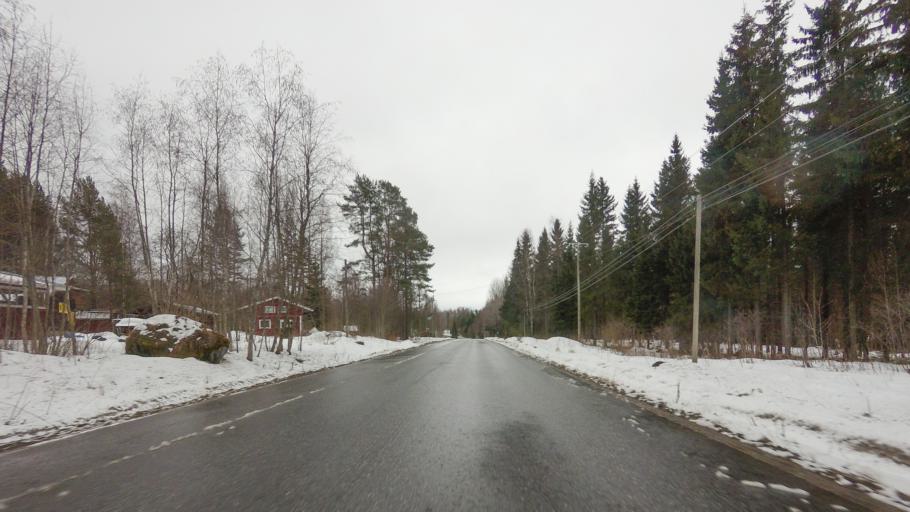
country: FI
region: Southern Savonia
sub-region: Savonlinna
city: Savonlinna
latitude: 61.9364
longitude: 28.8718
